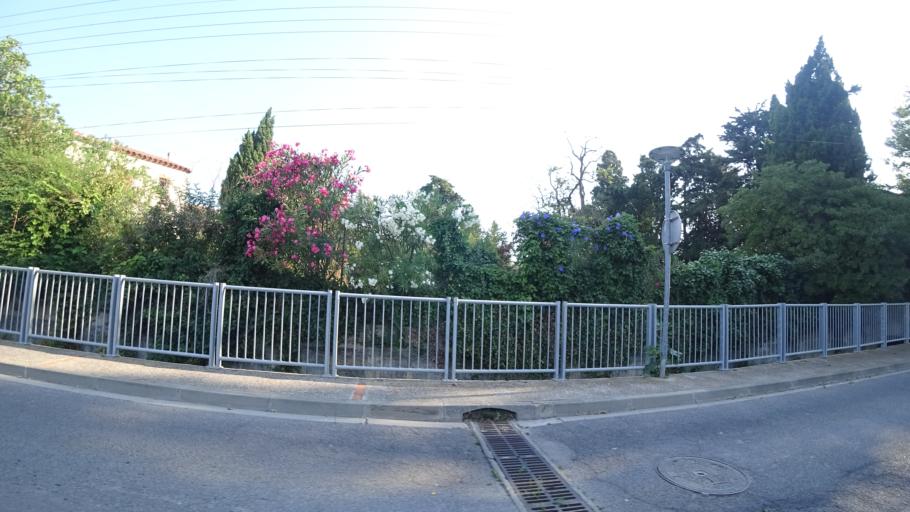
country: FR
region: Languedoc-Roussillon
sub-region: Departement des Pyrenees-Orientales
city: Sainte-Marie-Plage
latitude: 42.7283
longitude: 3.0150
